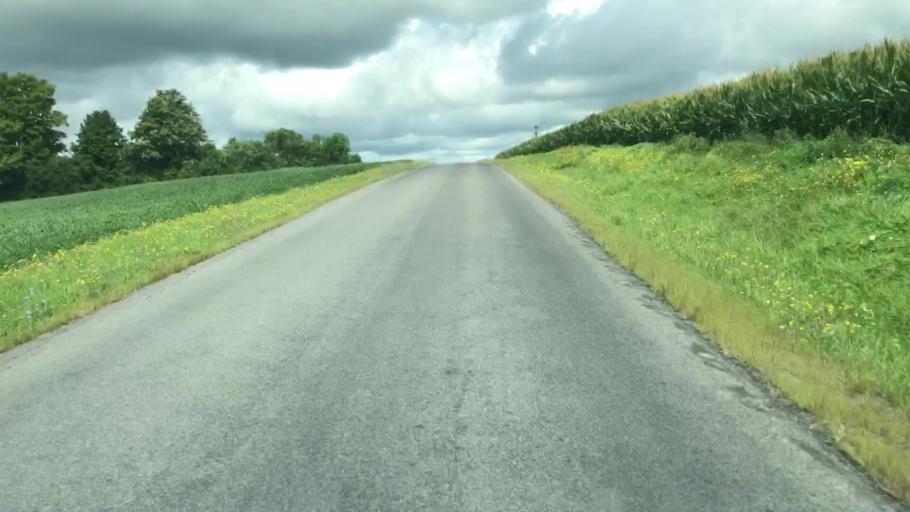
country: US
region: New York
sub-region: Onondaga County
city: Skaneateles
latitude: 42.9366
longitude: -76.4708
